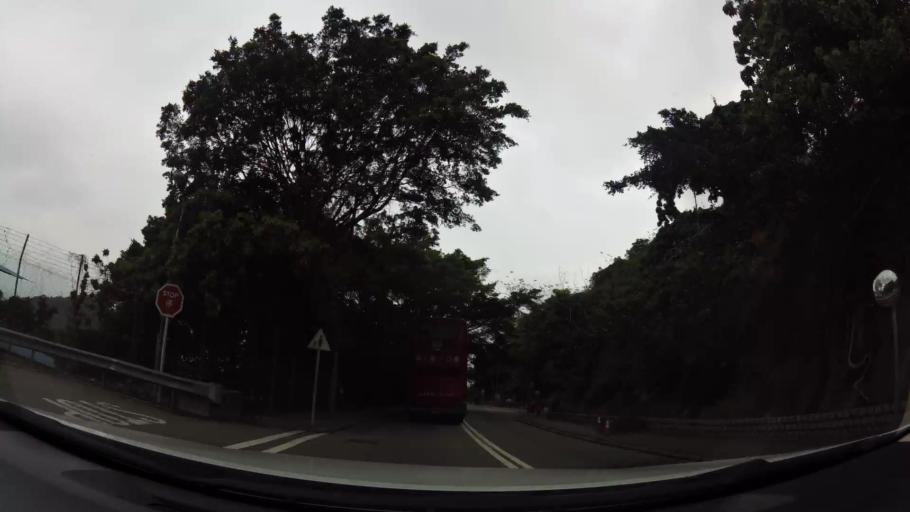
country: HK
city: Hong Kong
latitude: 22.2784
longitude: 114.1177
